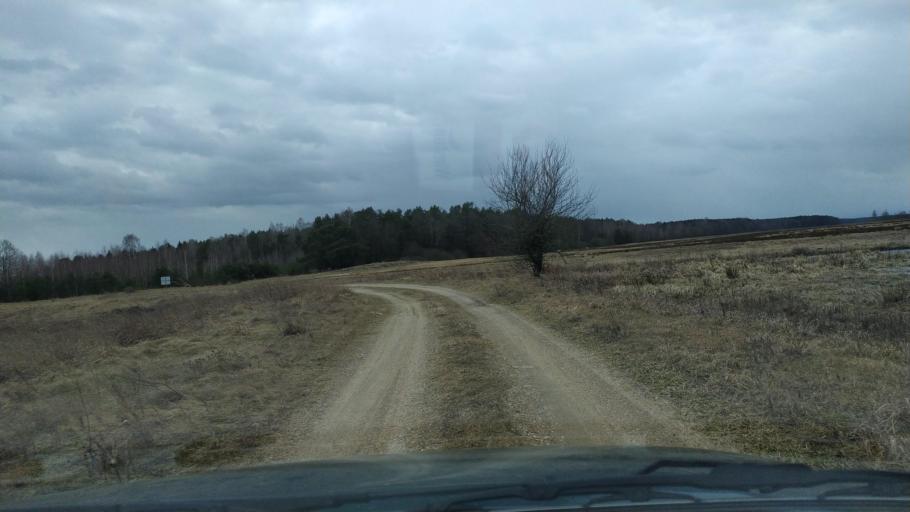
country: BY
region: Brest
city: Zhabinka
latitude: 52.4100
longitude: 24.0679
